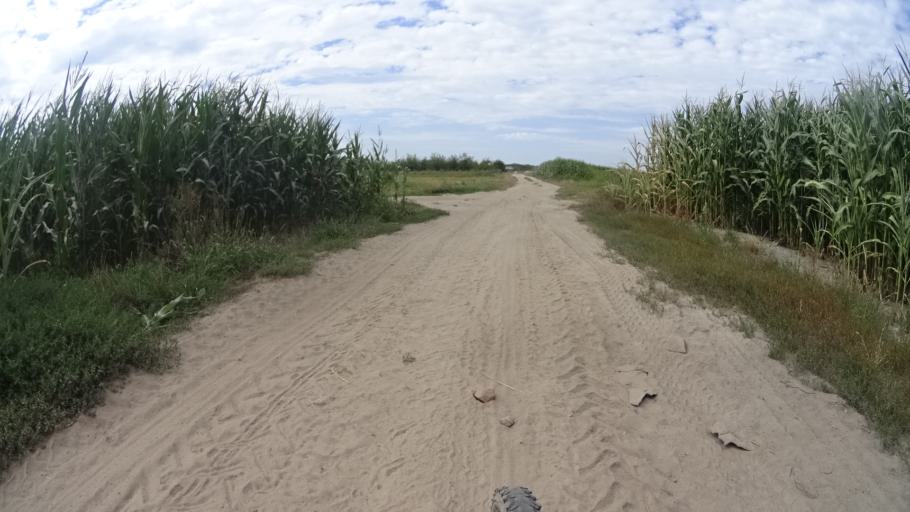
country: PL
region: Masovian Voivodeship
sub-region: Powiat bialobrzeski
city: Wysmierzyce
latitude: 51.6591
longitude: 20.7961
